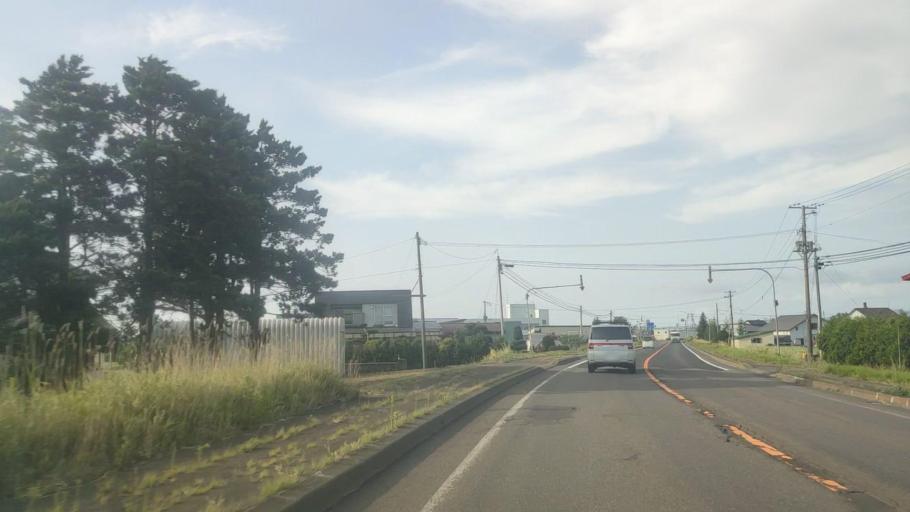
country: JP
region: Hokkaido
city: Iwamizawa
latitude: 43.0032
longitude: 141.7886
